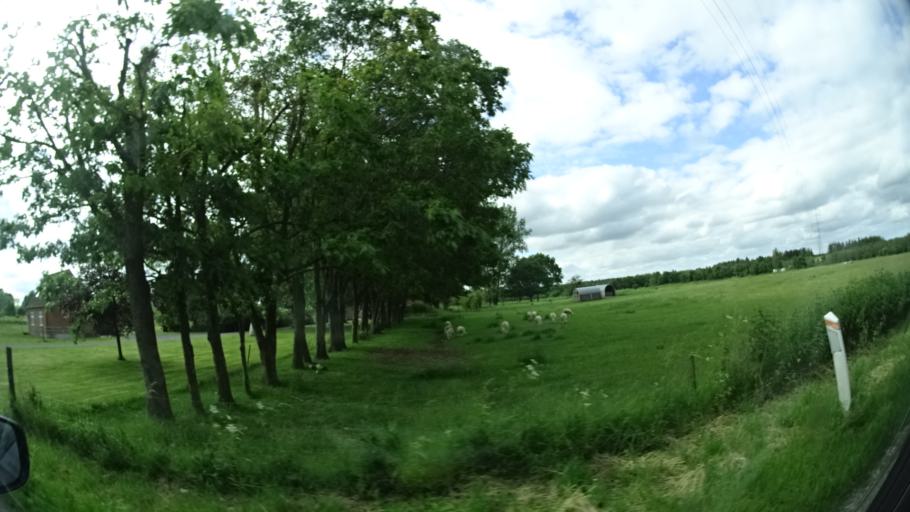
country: DK
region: Central Jutland
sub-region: Syddjurs Kommune
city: Ryomgard
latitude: 56.3536
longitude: 10.4854
